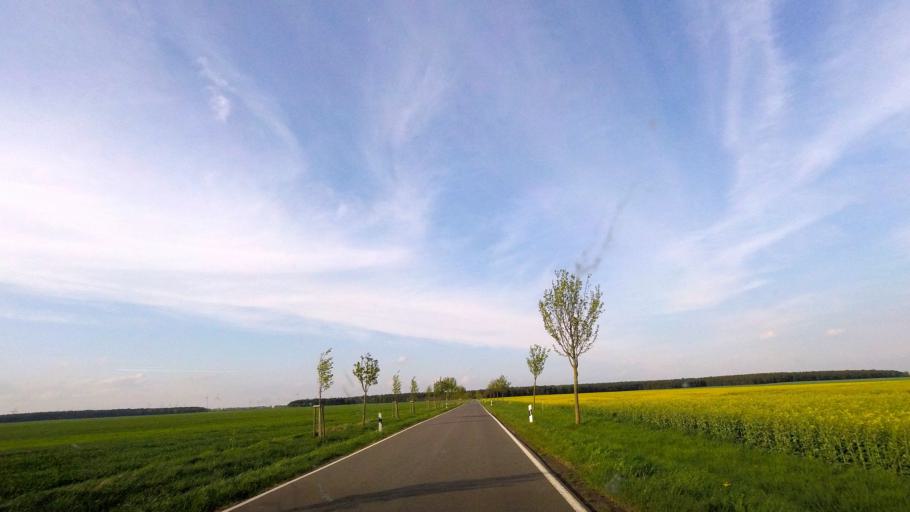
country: DE
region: Saxony-Anhalt
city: Zahna
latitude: 51.9513
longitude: 12.8438
